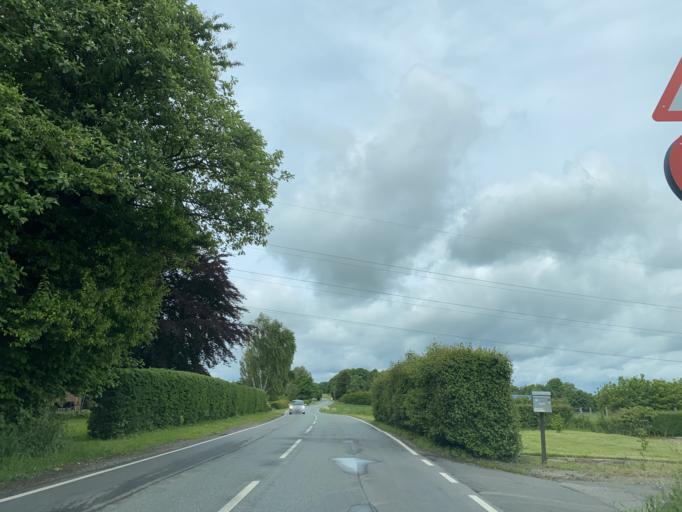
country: DK
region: Central Jutland
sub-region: Arhus Kommune
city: Trige
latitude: 56.1890
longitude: 10.1484
